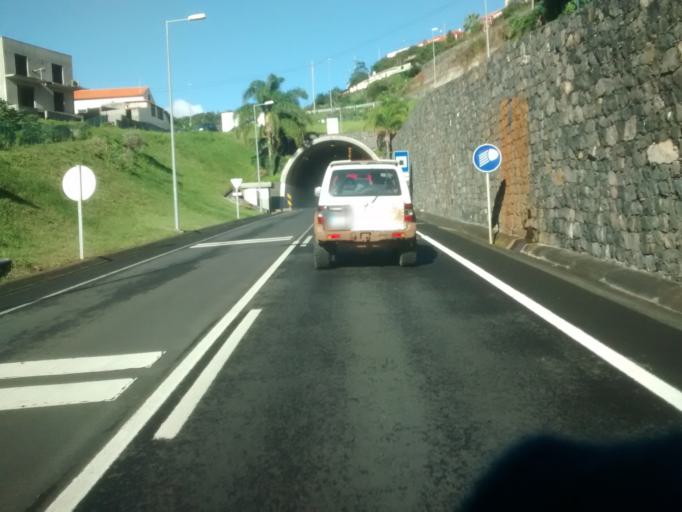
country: PT
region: Madeira
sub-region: Machico
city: Machico
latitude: 32.7308
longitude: -16.7823
